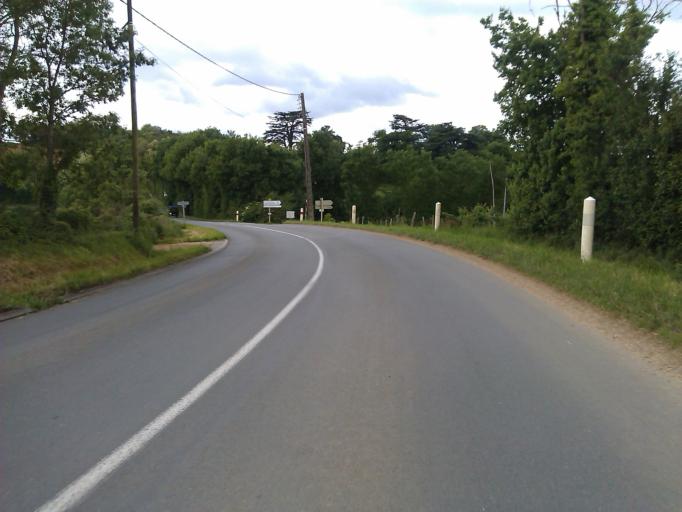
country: FR
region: Poitou-Charentes
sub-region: Departement de la Charente
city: Nanteuil-en-Vallee
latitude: 45.9855
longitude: 0.3531
